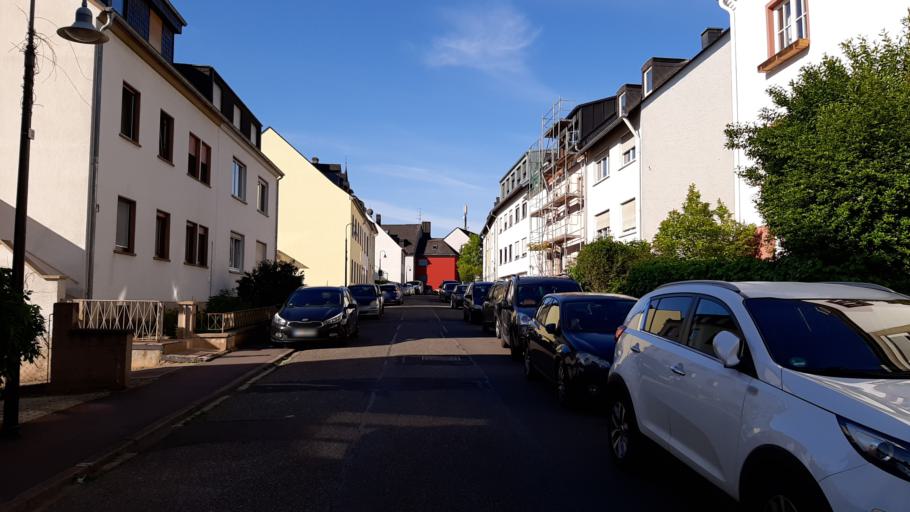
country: DE
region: Rheinland-Pfalz
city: Trier
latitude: 49.7430
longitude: 6.6088
